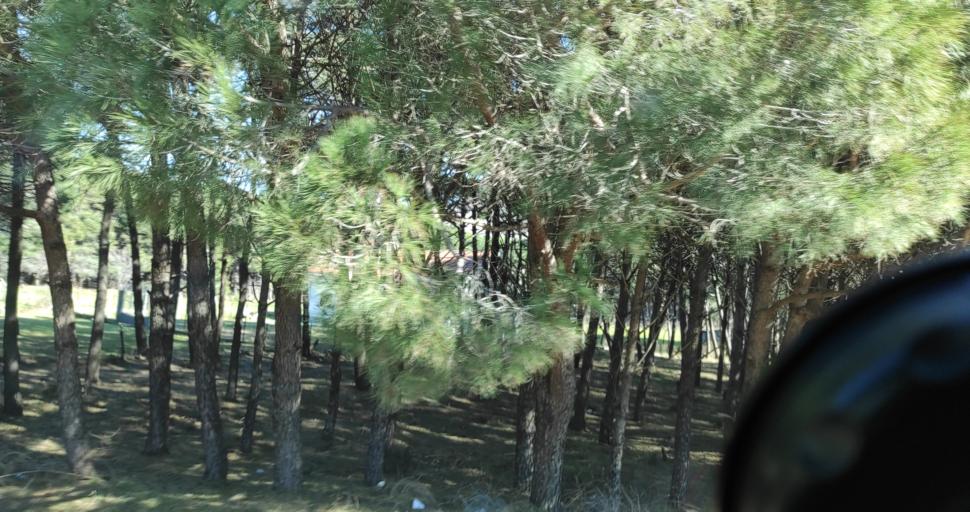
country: AL
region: Shkoder
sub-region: Rrethi i Shkodres
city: Velipoje
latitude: 41.8635
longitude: 19.4443
